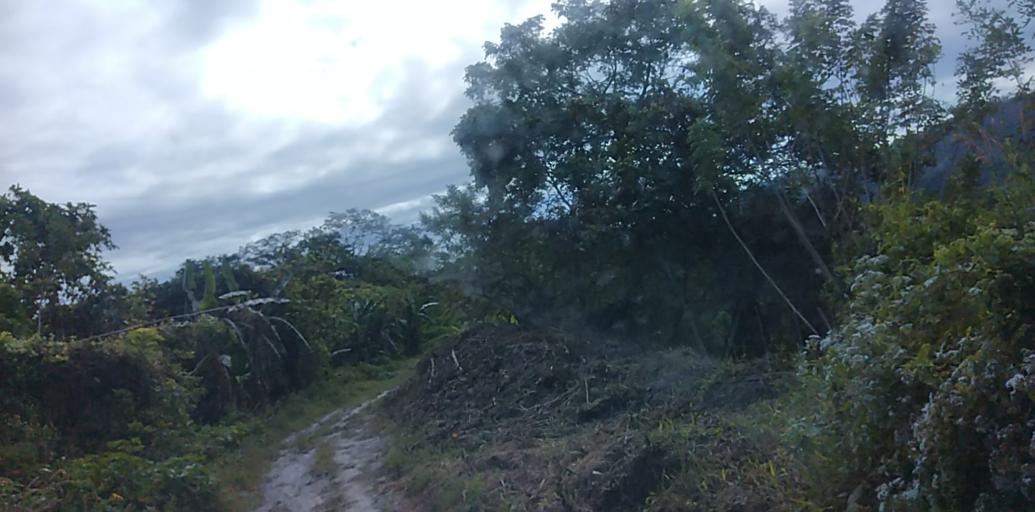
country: PH
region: Central Luzon
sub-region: Province of Pampanga
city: Babo-Pangulo
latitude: 15.1505
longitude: 120.4471
